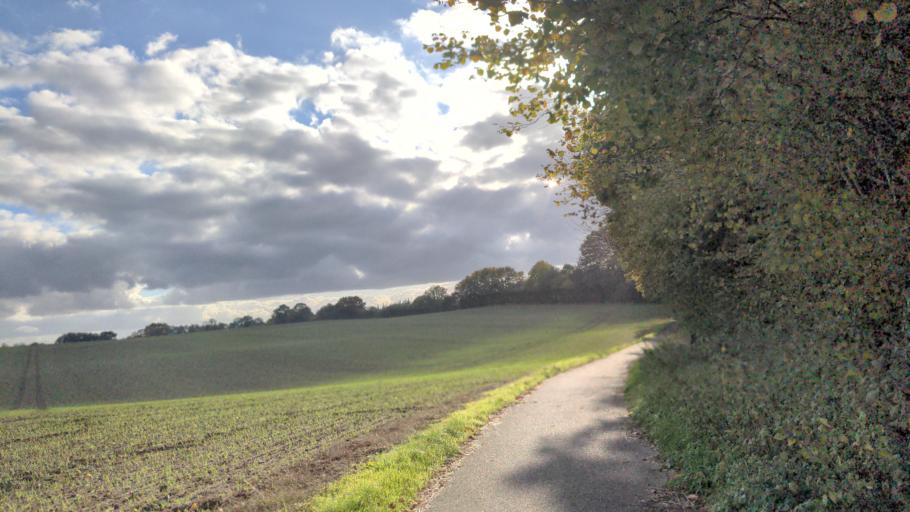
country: DE
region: Schleswig-Holstein
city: Bosau
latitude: 54.1164
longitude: 10.4432
